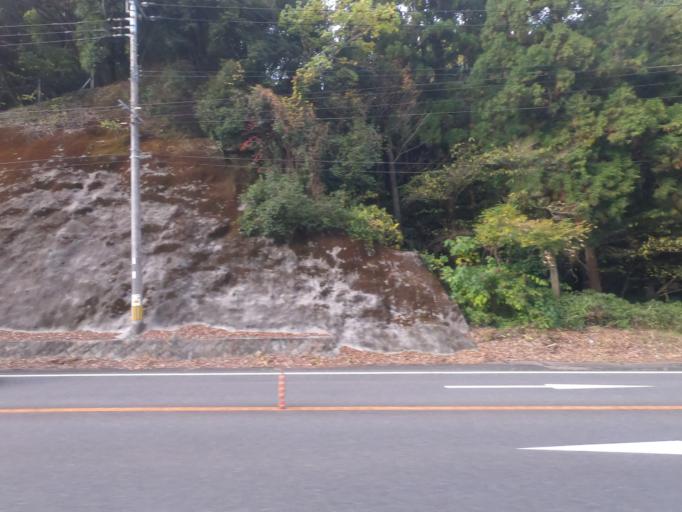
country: JP
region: Kumamoto
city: Minamata
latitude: 32.2469
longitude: 130.4963
